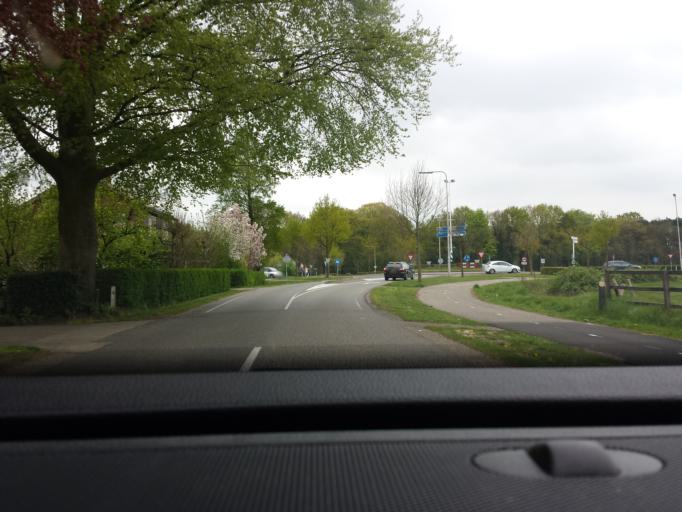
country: NL
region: Gelderland
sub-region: Gemeente Bronckhorst
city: Zelhem
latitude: 52.0138
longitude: 6.3420
